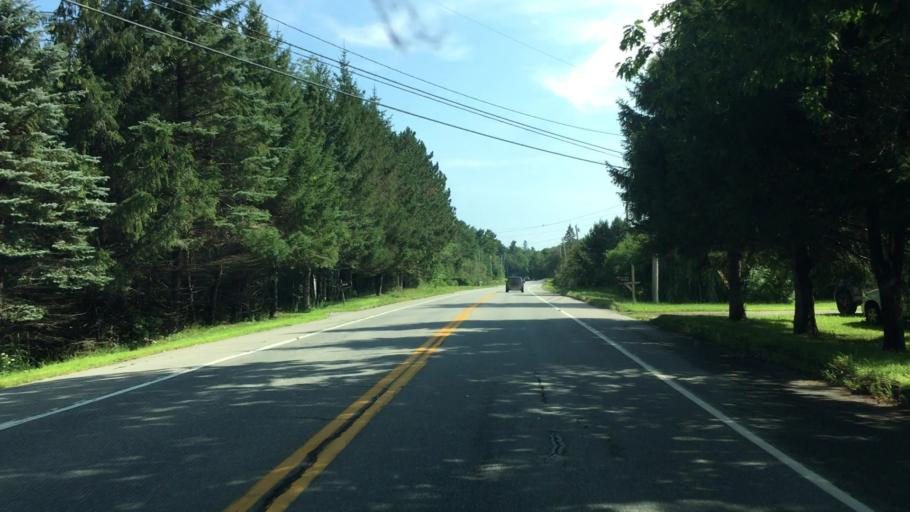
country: US
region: Maine
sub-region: Waldo County
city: Winterport
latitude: 44.6859
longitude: -68.8455
